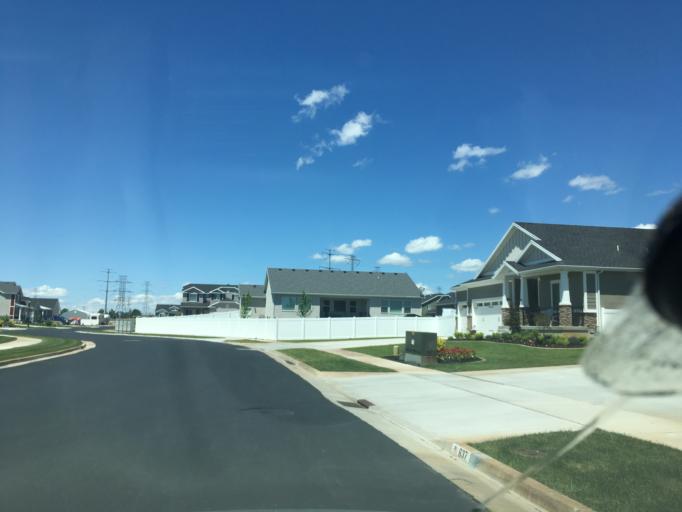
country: US
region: Utah
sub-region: Davis County
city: Layton
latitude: 41.0508
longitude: -112.0057
